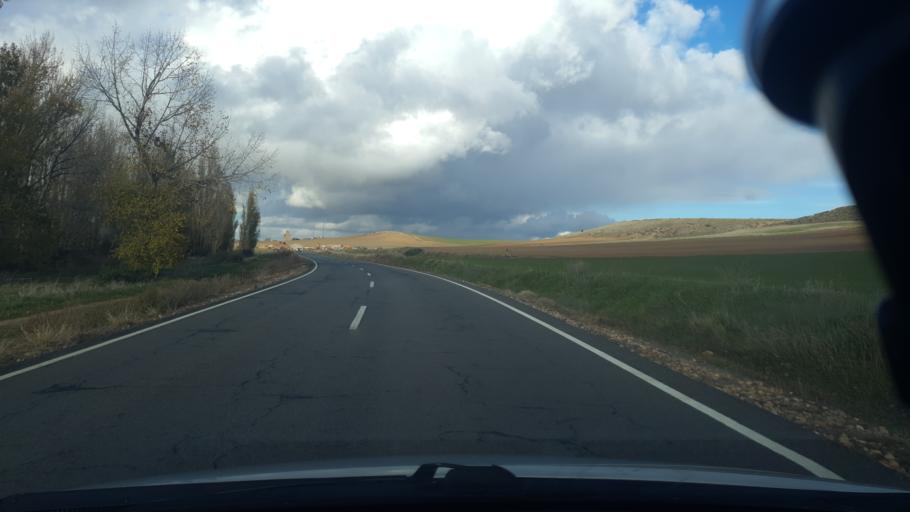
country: ES
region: Castille and Leon
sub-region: Provincia de Avila
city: Hernansancho
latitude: 40.8419
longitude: -4.7295
